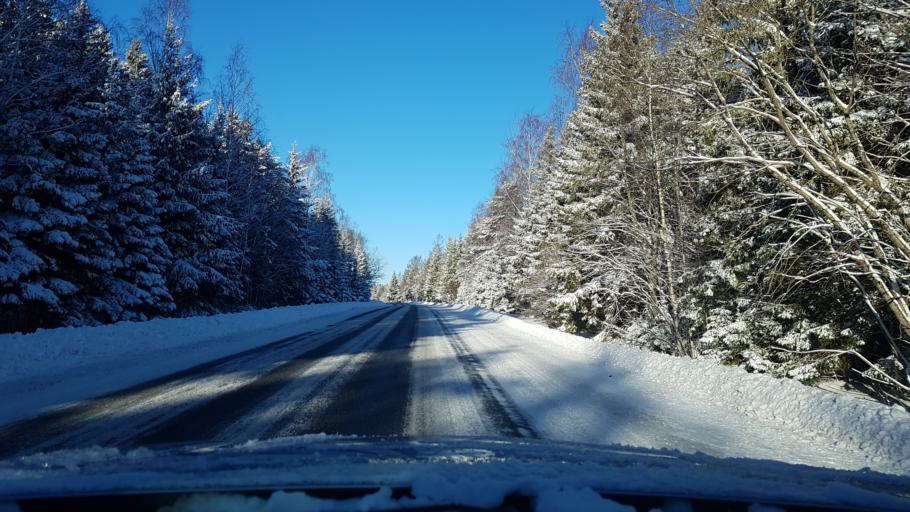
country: EE
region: Hiiumaa
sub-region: Kaerdla linn
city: Kardla
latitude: 58.9743
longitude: 22.8203
